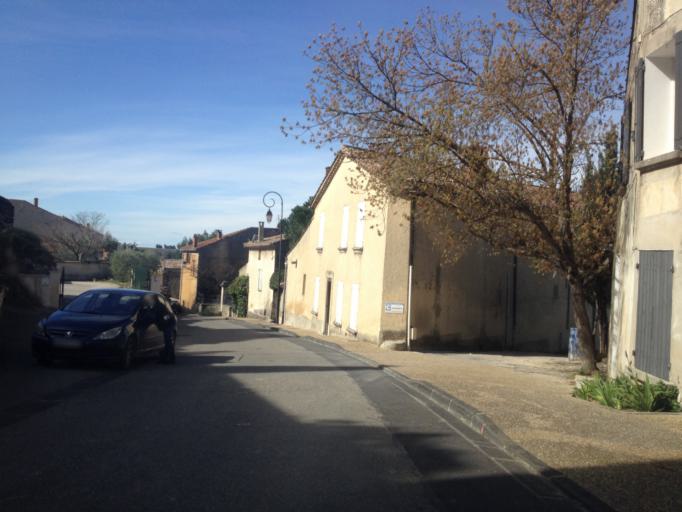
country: FR
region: Provence-Alpes-Cote d'Azur
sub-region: Departement du Vaucluse
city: Sablet
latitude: 44.1929
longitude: 5.0057
